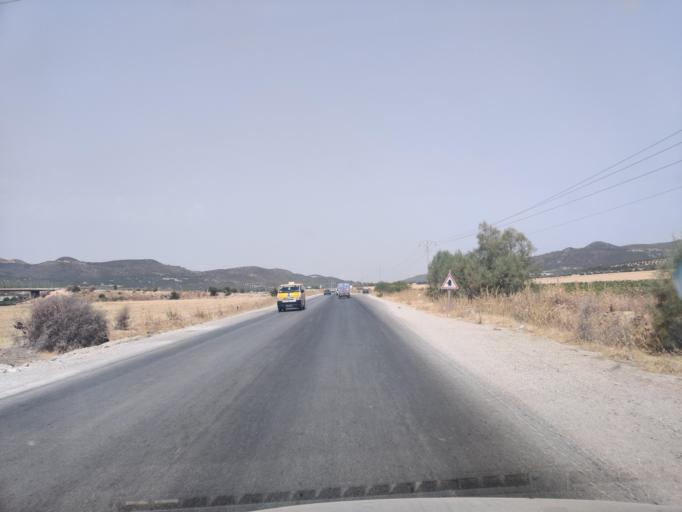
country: TN
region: Tunis
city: Hammam-Lif
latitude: 36.6194
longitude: 10.4117
